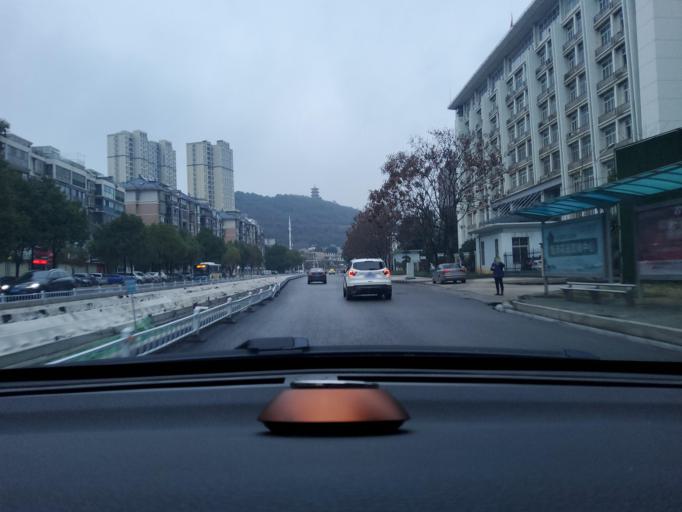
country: CN
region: Hubei
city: Tuanchengshan
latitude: 30.1951
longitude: 115.0165
